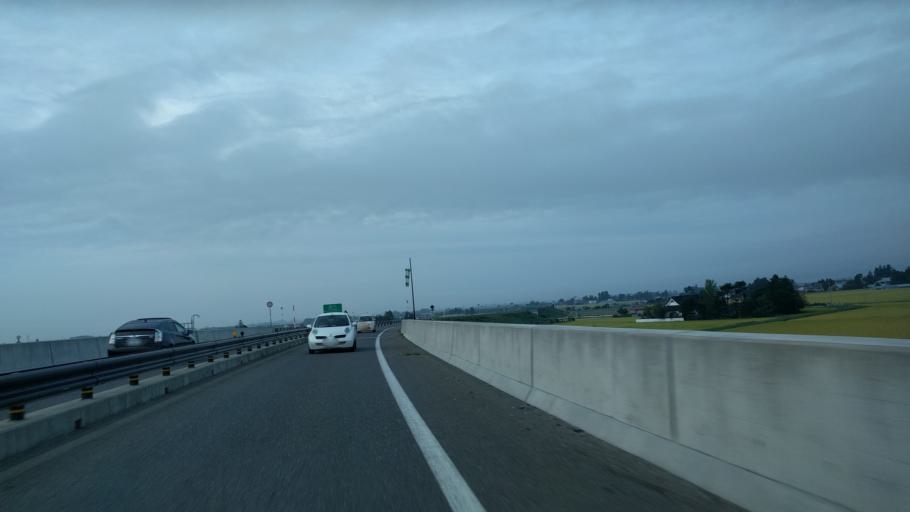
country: JP
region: Fukushima
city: Kitakata
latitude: 37.6119
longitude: 139.8821
